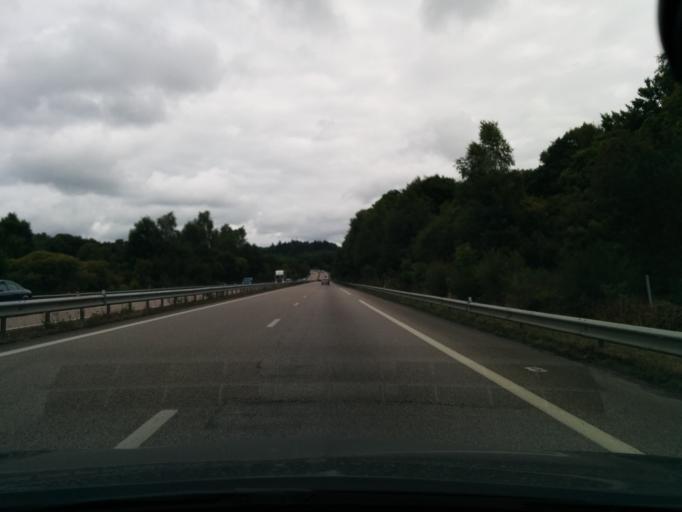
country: FR
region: Limousin
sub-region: Departement de la Haute-Vienne
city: Bonnac-la-Cote
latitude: 45.9420
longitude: 1.3073
